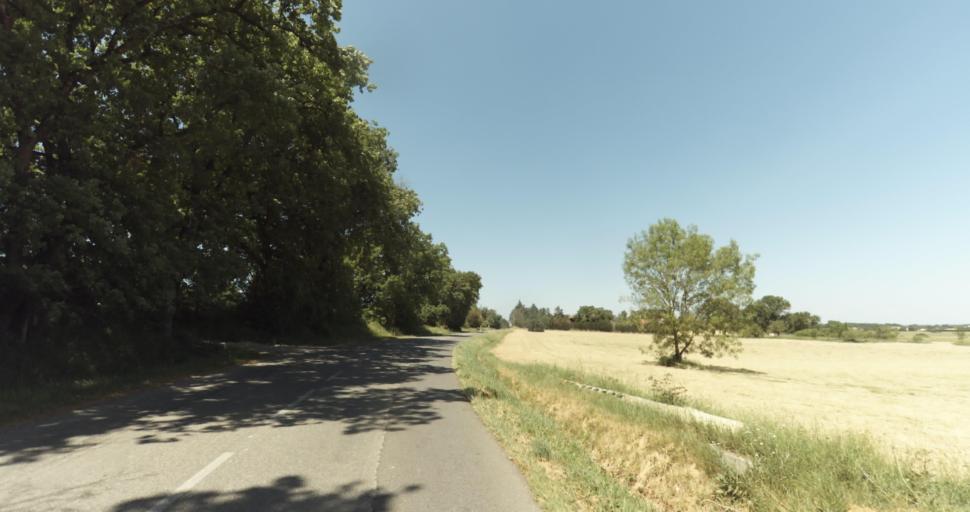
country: FR
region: Midi-Pyrenees
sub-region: Departement de la Haute-Garonne
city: Levignac
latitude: 43.6307
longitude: 1.1814
